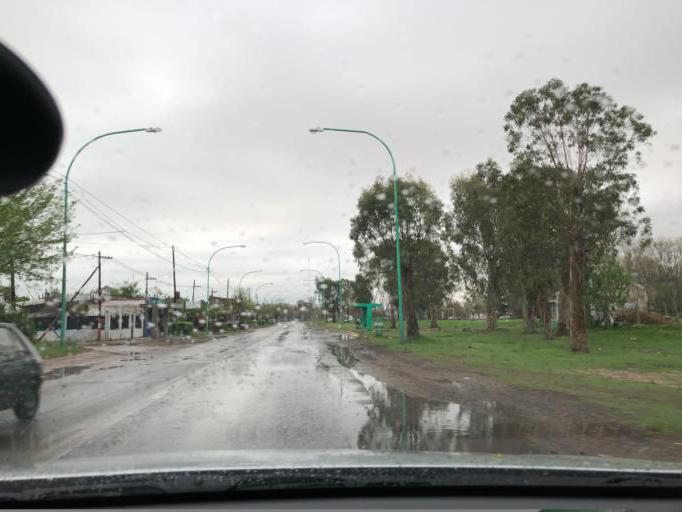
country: AR
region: Buenos Aires
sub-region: Partido de Ensenada
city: Ensenada
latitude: -34.8358
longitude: -57.9454
